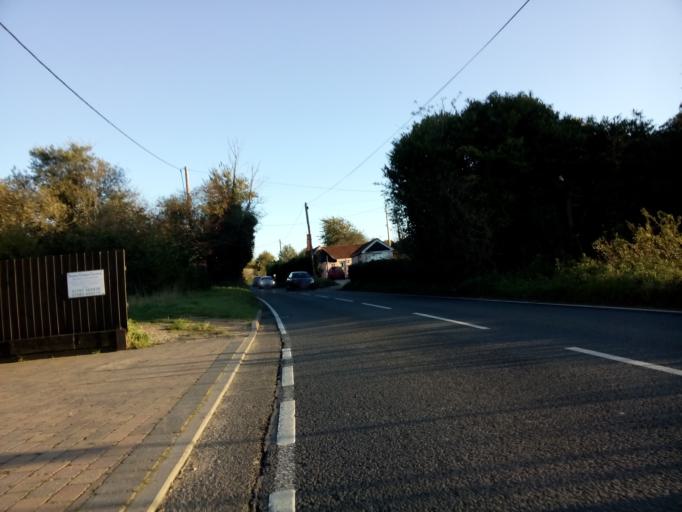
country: GB
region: England
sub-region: Suffolk
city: Sudbury
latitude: 52.0120
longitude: 0.7485
